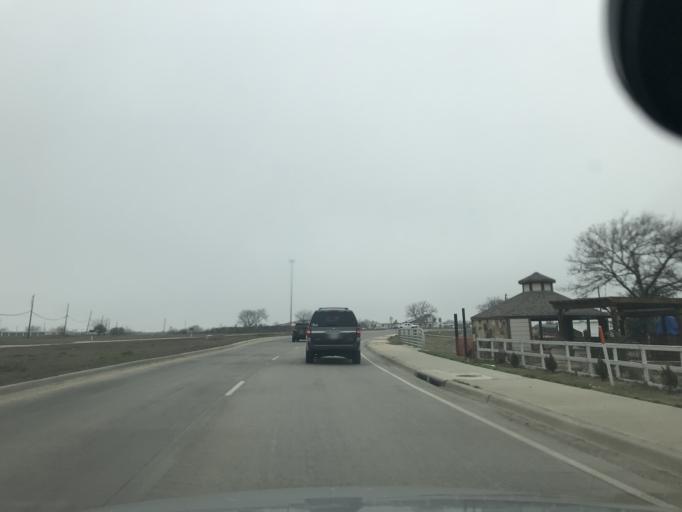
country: US
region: Texas
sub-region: Collin County
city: Saint Paul
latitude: 33.0517
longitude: -96.5625
